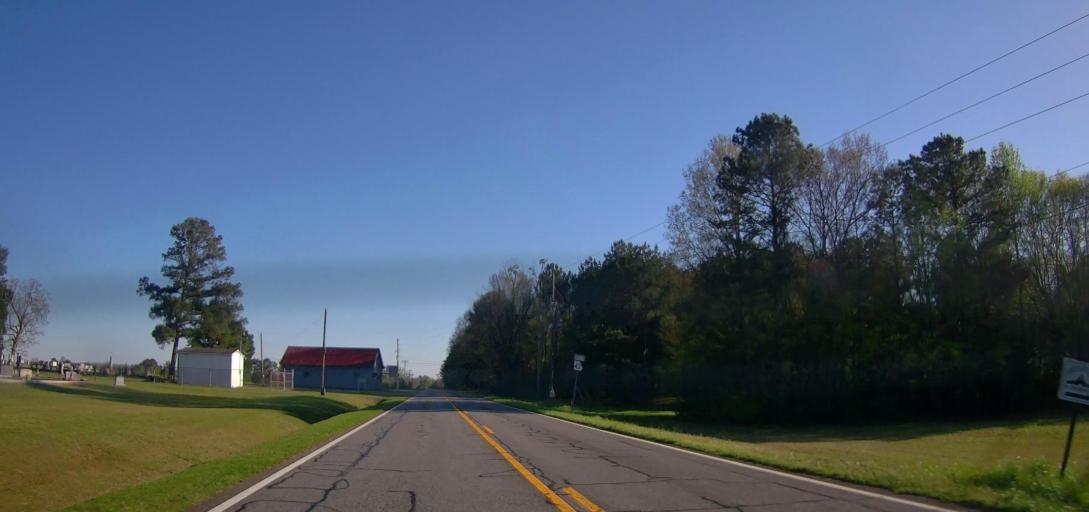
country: US
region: Georgia
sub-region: Butts County
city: Indian Springs
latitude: 33.1775
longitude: -83.9591
